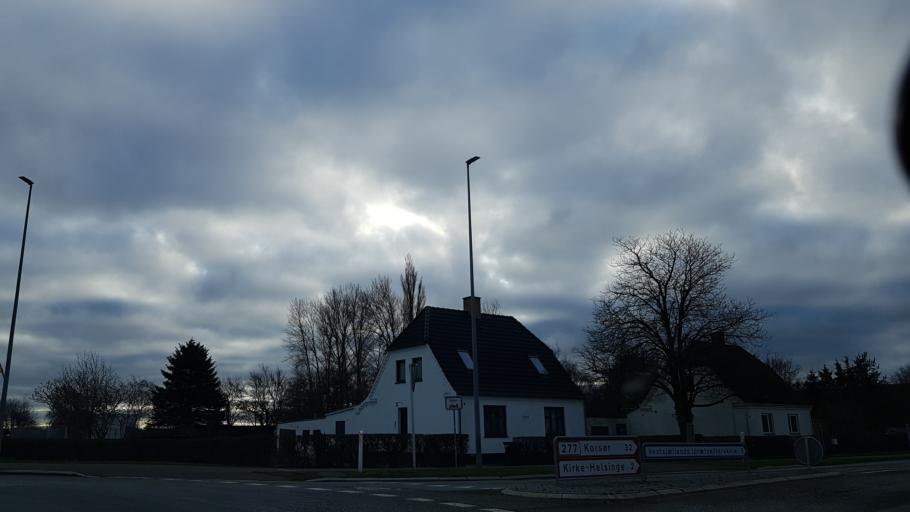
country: DK
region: Zealand
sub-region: Kalundborg Kommune
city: Gorlev
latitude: 55.5353
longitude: 11.2219
